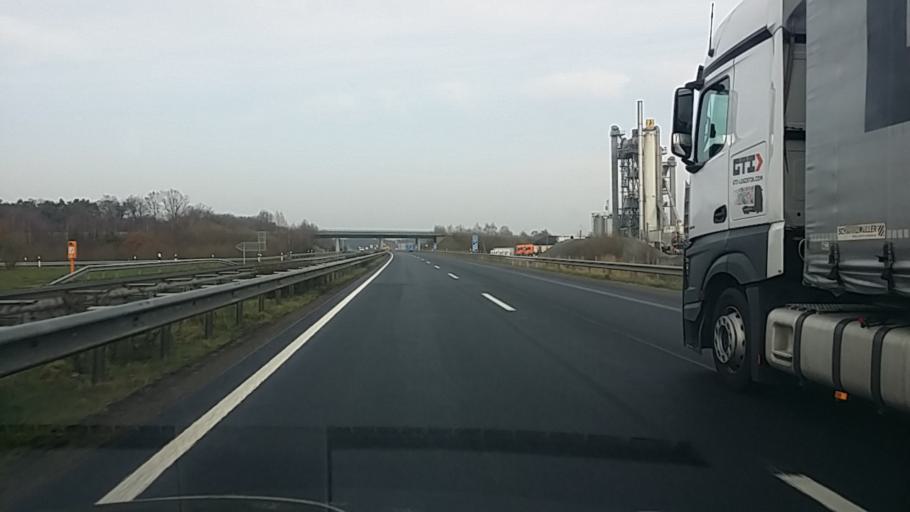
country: DE
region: Lower Saxony
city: Schuttorf
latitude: 52.3539
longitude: 7.2585
